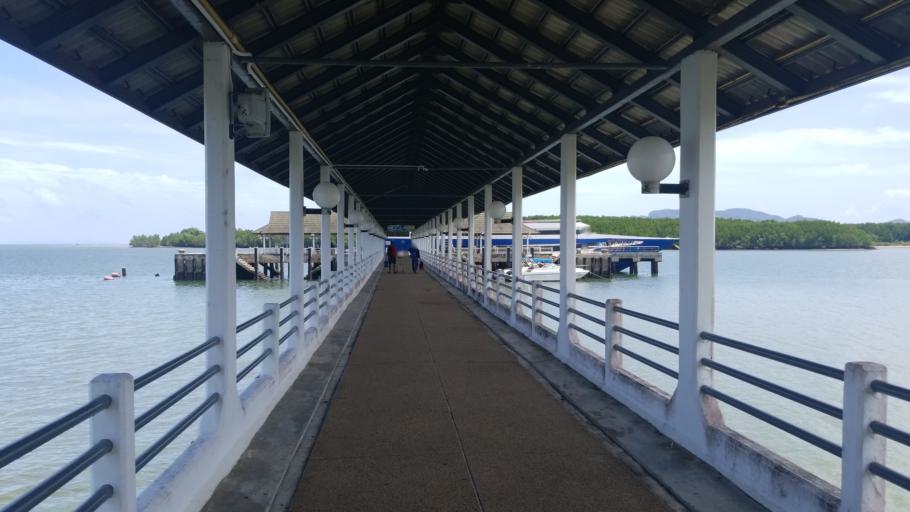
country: TH
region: Krabi
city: Krabi
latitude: 8.0464
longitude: 98.9065
